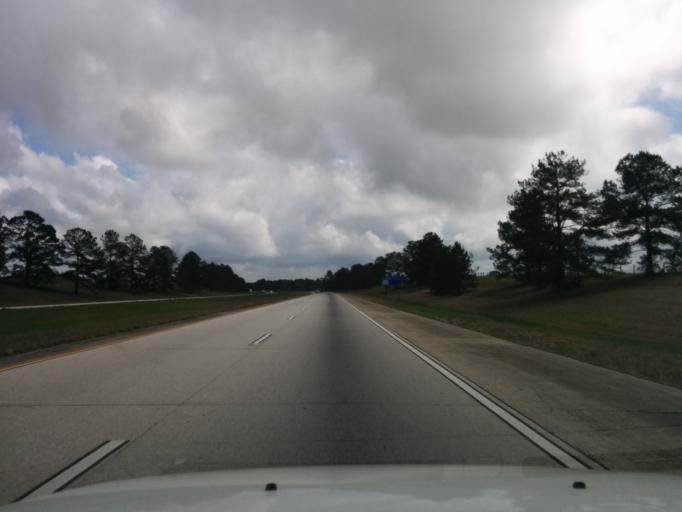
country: US
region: Georgia
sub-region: Evans County
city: Claxton
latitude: 32.3147
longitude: -81.9038
